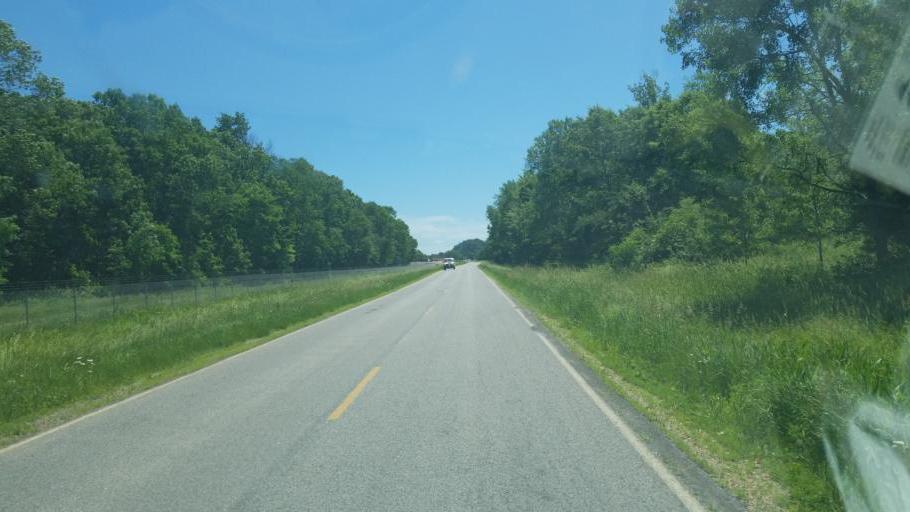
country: US
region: Wisconsin
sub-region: Juneau County
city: New Lisbon
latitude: 43.9356
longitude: -90.2812
